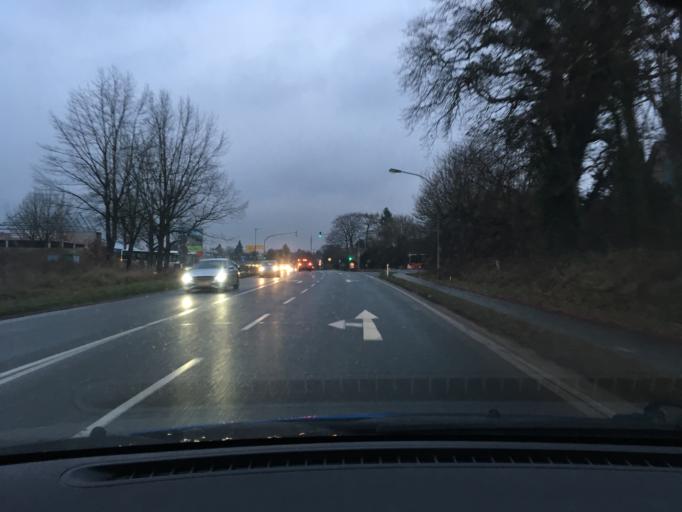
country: DE
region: Lower Saxony
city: Seevetal
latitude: 53.3988
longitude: 9.9769
